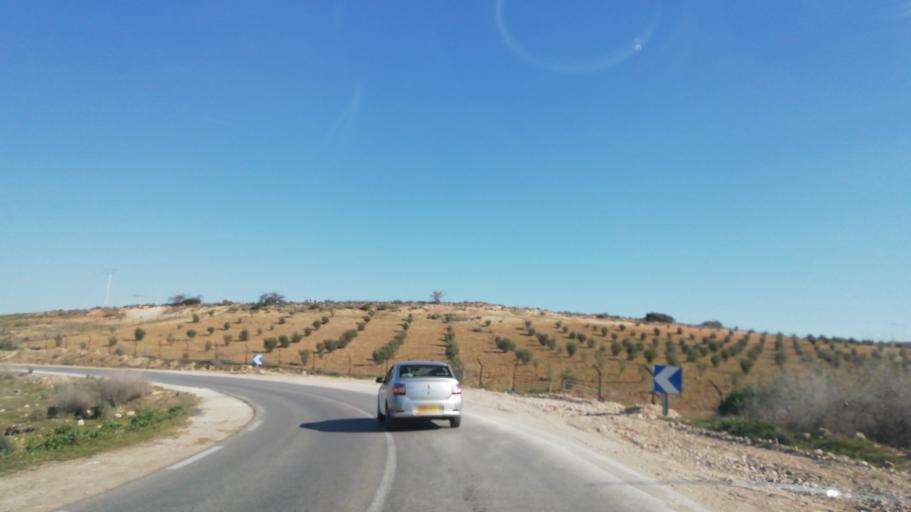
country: DZ
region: Tlemcen
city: Nedroma
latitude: 34.8325
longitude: -1.6869
